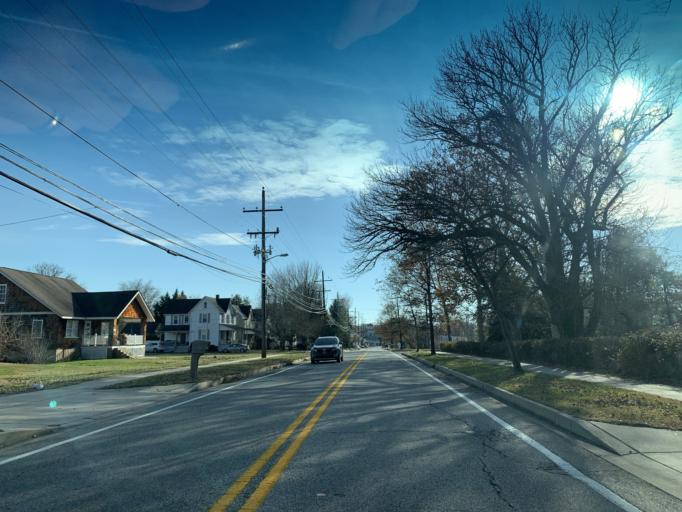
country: US
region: Maryland
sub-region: Cecil County
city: Perryville
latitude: 39.5641
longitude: -76.0710
